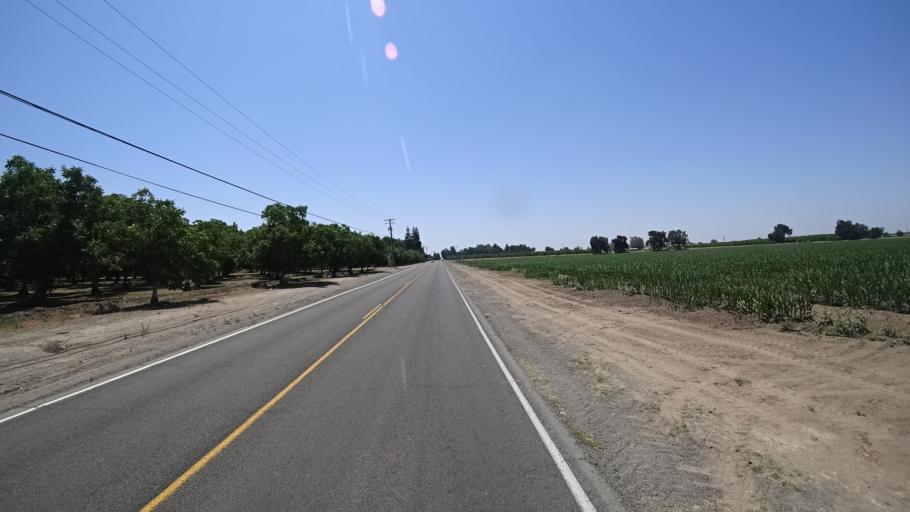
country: US
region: California
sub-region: Fresno County
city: Laton
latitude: 36.4186
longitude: -119.6863
